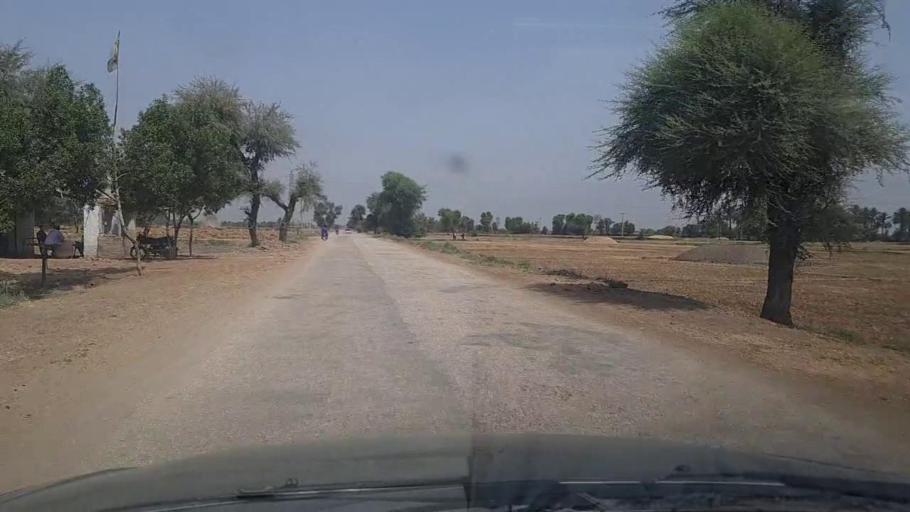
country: PK
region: Sindh
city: Setharja Old
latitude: 27.1516
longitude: 68.5228
